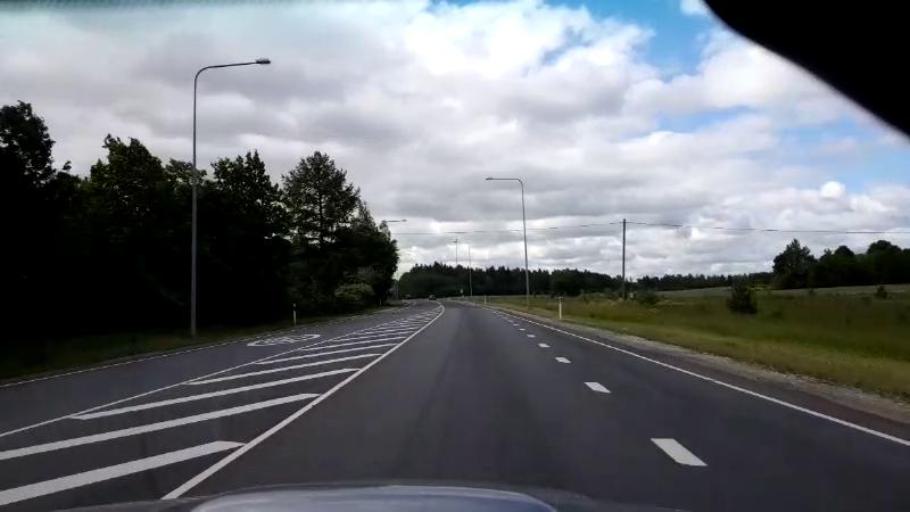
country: EE
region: Raplamaa
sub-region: Maerjamaa vald
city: Marjamaa
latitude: 58.9175
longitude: 24.4570
